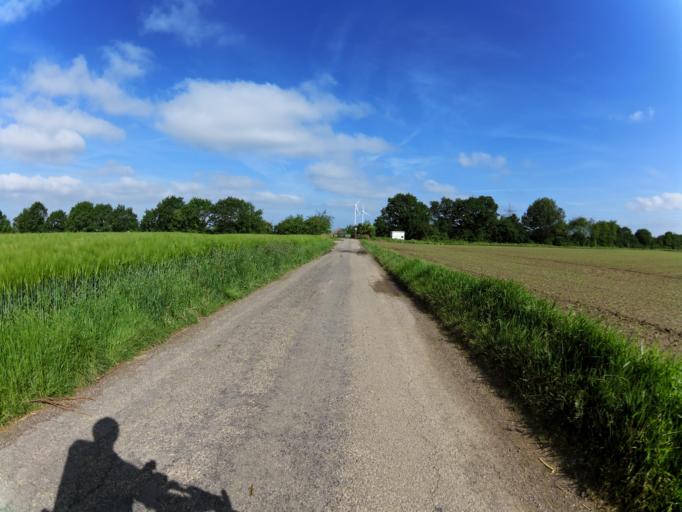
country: DE
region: North Rhine-Westphalia
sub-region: Regierungsbezirk Koln
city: Linnich
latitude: 51.0018
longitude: 6.2238
